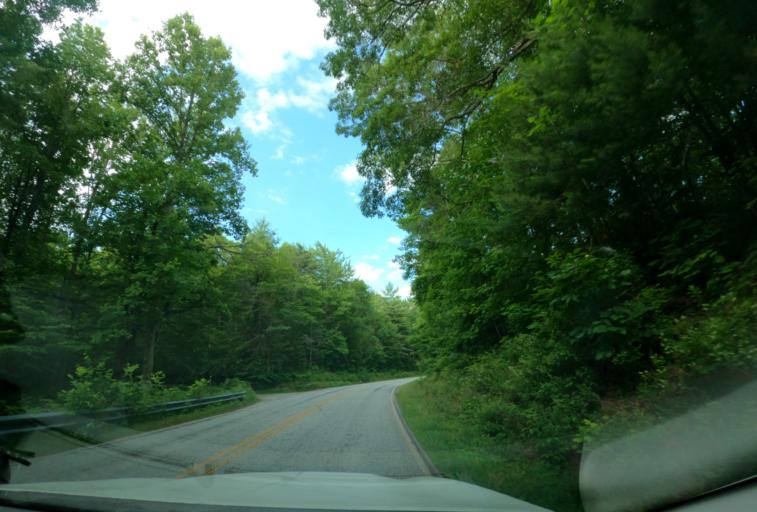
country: US
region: North Carolina
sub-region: Transylvania County
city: Brevard
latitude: 35.1724
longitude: -82.9270
